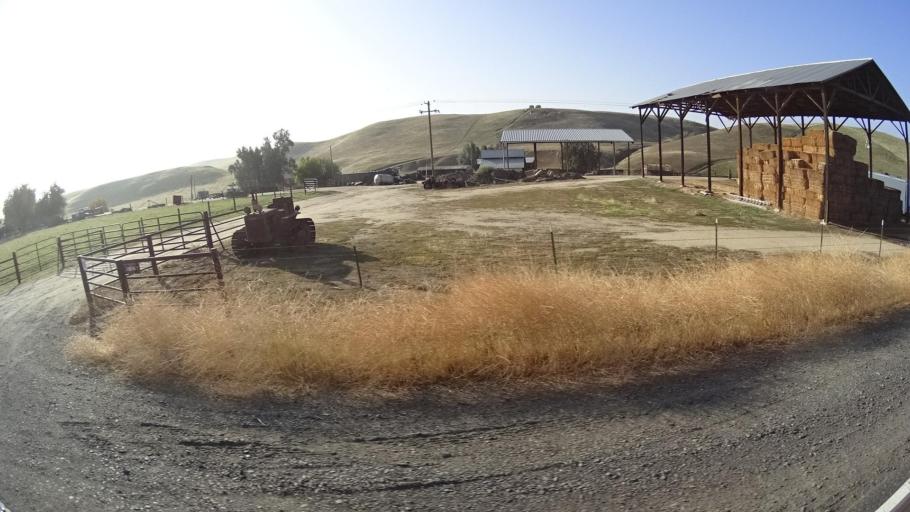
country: US
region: California
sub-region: Tulare County
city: Richgrove
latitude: 35.7459
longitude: -118.9789
